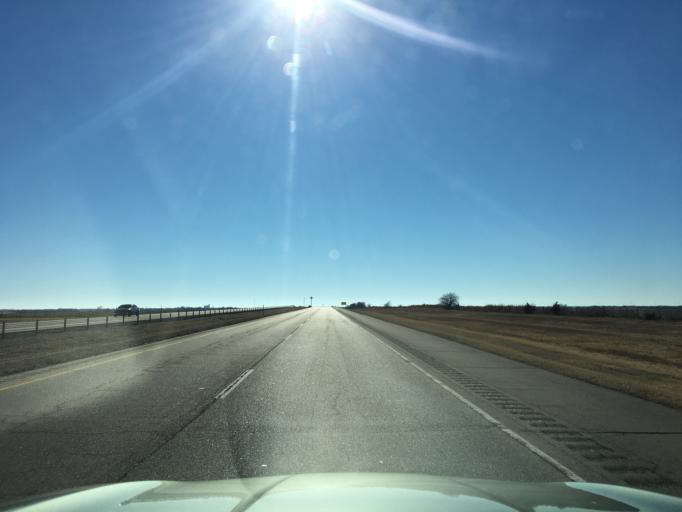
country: US
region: Oklahoma
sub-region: Kay County
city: Blackwell
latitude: 36.9699
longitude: -97.3458
